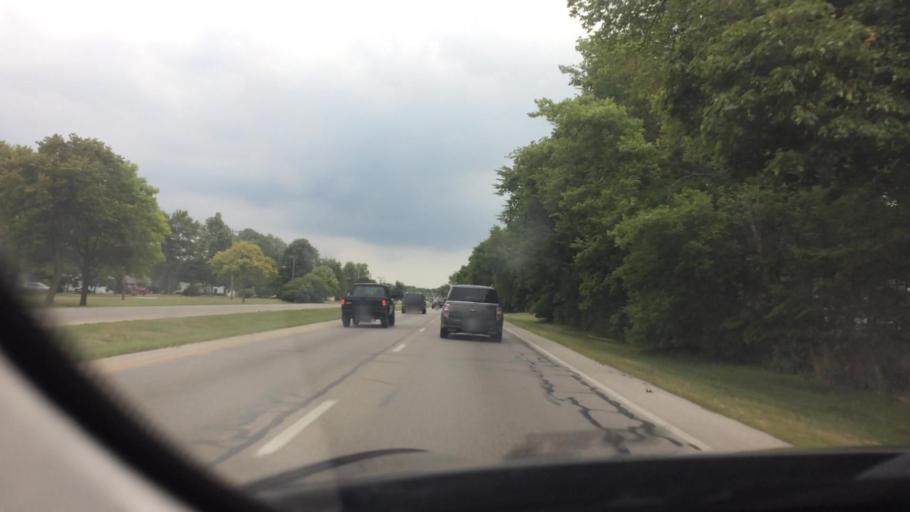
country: US
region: Ohio
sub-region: Wood County
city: Perrysburg
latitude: 41.5781
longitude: -83.6292
